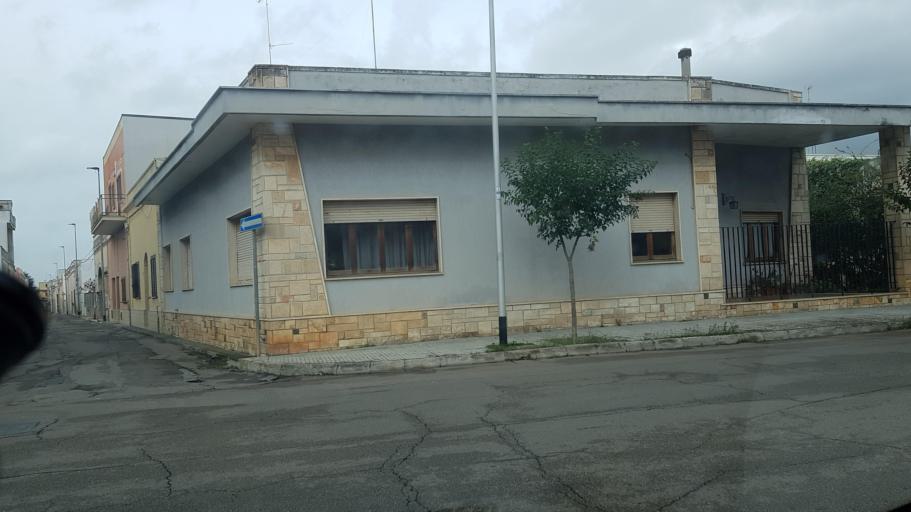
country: IT
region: Apulia
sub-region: Provincia di Lecce
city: Carmiano
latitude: 40.3421
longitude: 18.0469
